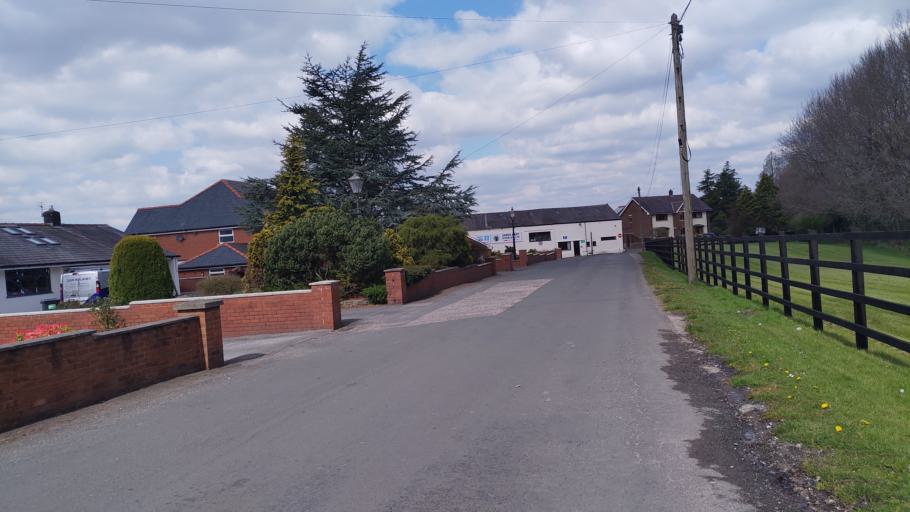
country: GB
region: England
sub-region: Lancashire
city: Coppull
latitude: 53.6418
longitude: -2.6509
